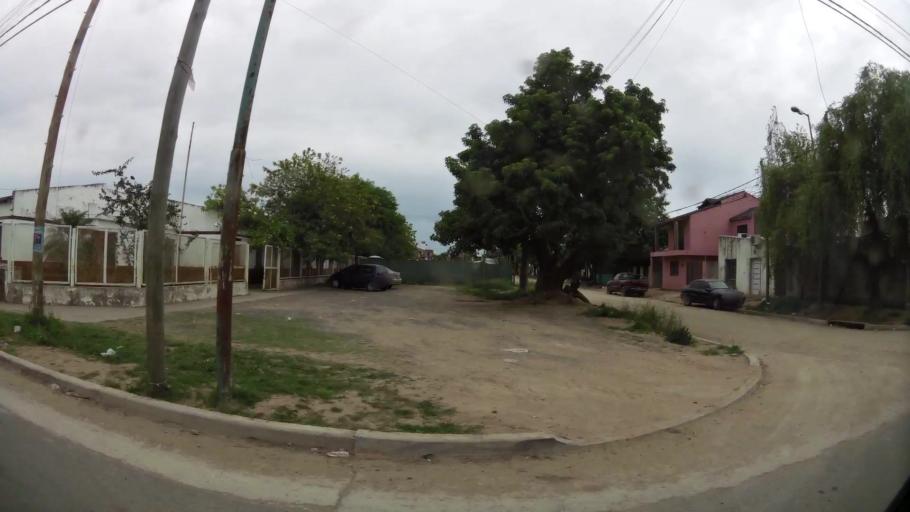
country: AR
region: Buenos Aires
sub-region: Partido de Zarate
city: Zarate
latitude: -34.1128
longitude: -59.0271
